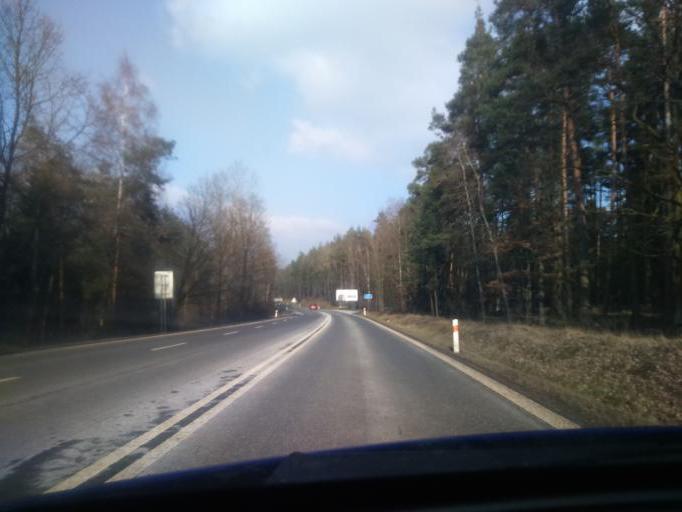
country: CZ
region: Plzensky
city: Holysov
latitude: 49.6112
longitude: 13.1280
